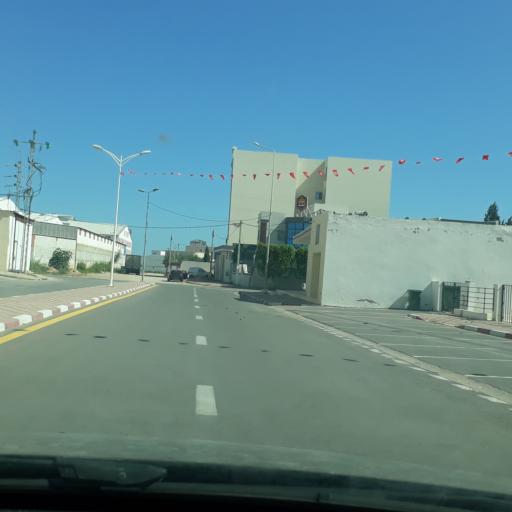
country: TN
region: Safaqis
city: Al Qarmadah
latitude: 34.8344
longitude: 10.7622
